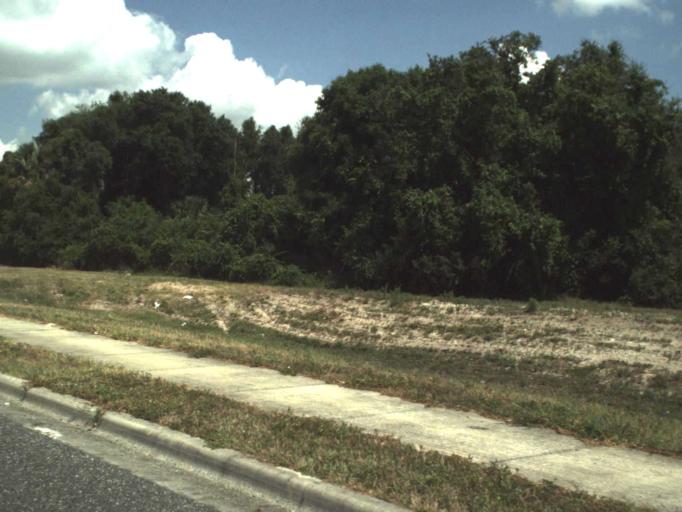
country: US
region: Florida
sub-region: Lake County
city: Silver Lake
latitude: 28.8280
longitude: -81.8029
